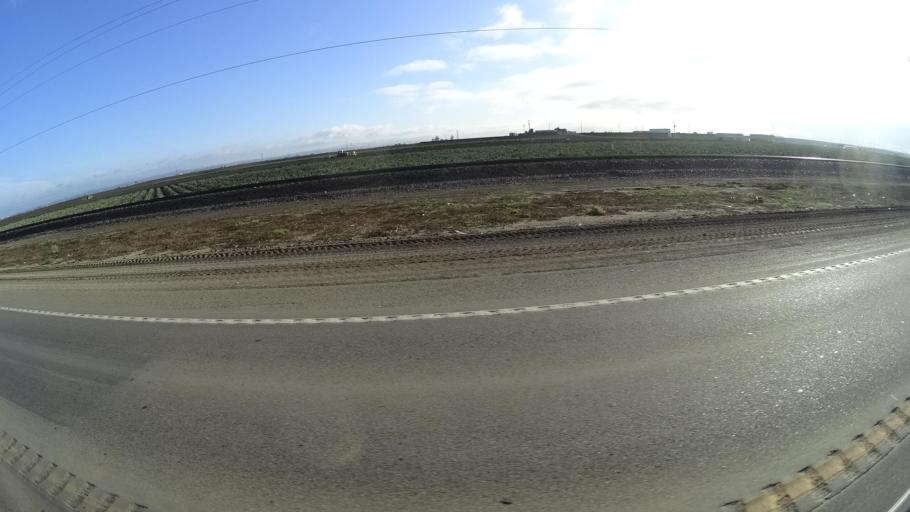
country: US
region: California
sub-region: Monterey County
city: Boronda
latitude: 36.7105
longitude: -121.7135
